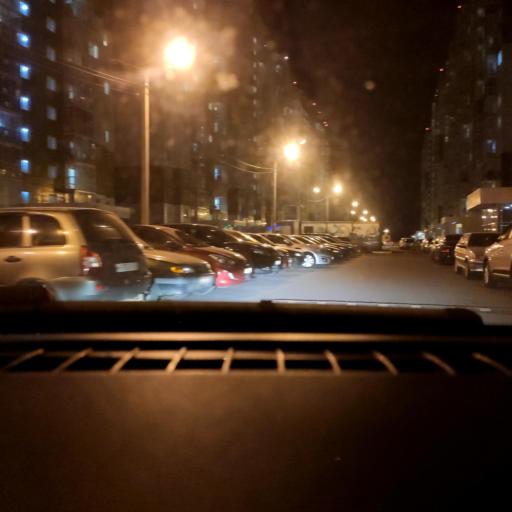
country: RU
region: Voronezj
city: Maslovka
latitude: 51.6340
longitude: 39.2964
